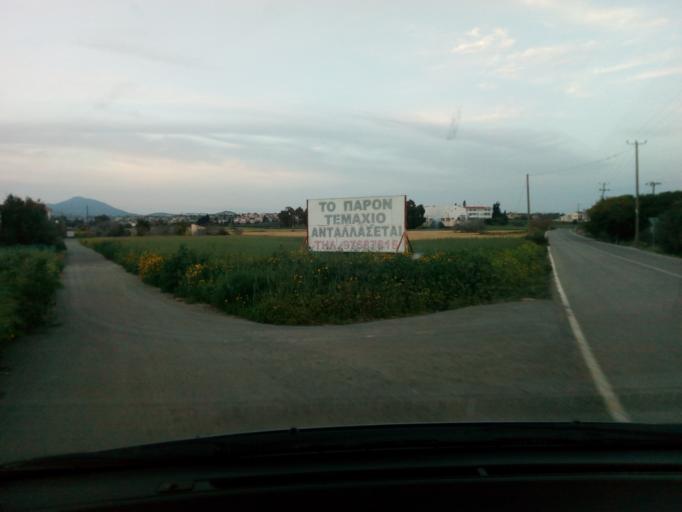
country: CY
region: Larnaka
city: Tersefanou
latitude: 34.7939
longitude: 33.4899
